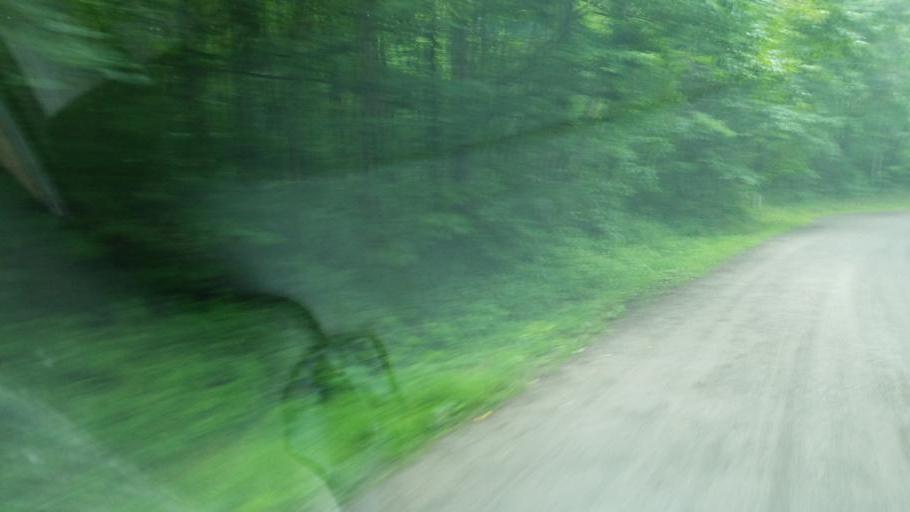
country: US
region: Ohio
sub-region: Columbiana County
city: Salineville
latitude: 40.5408
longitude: -80.8324
